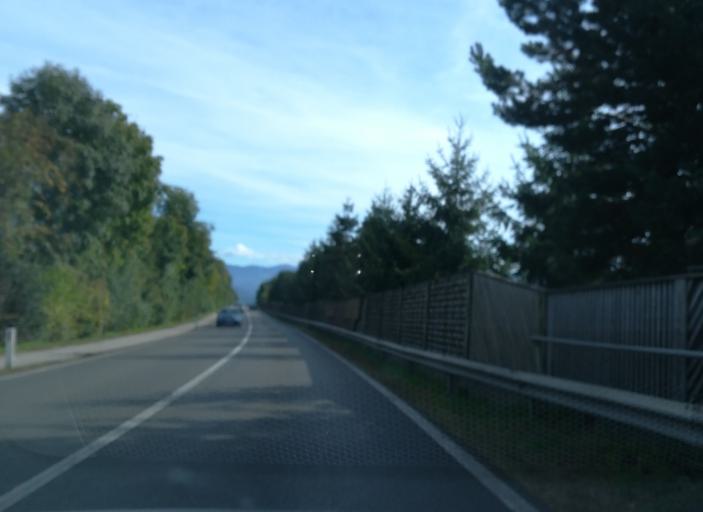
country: AT
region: Styria
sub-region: Politischer Bezirk Murtal
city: Zeltweg
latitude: 47.1946
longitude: 14.7499
